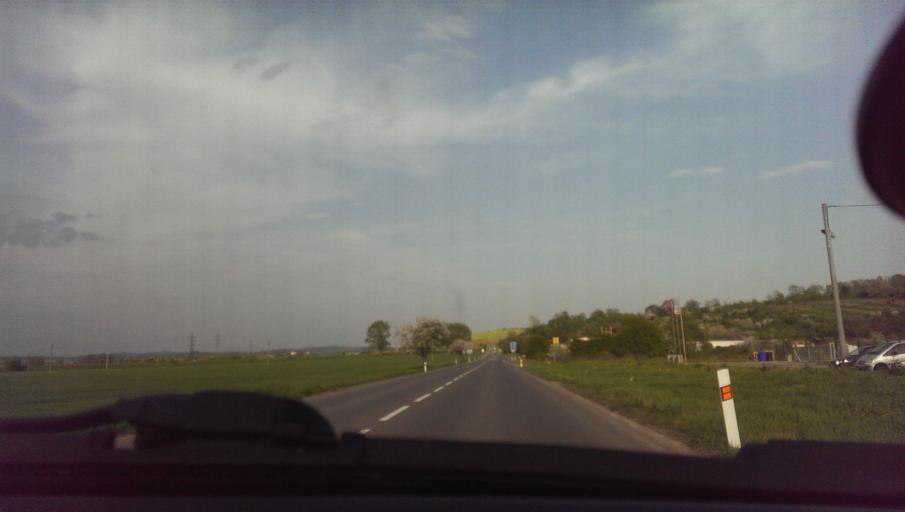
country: CZ
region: Zlin
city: Knezpole
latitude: 49.0905
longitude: 17.5072
